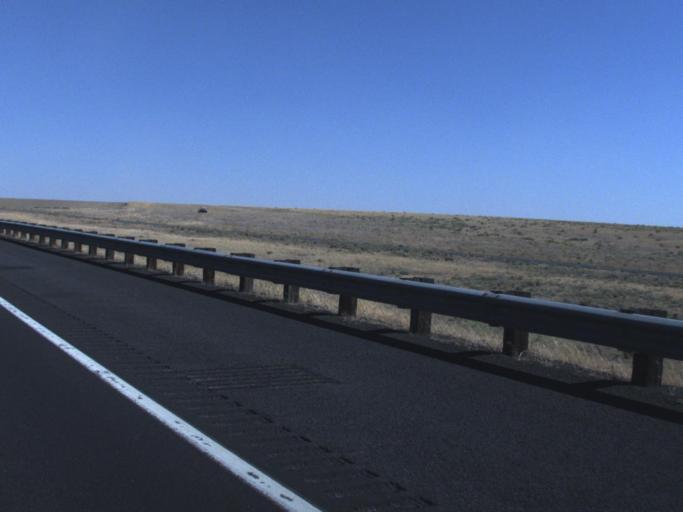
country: US
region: Washington
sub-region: Adams County
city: Ritzville
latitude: 47.0871
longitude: -118.7137
